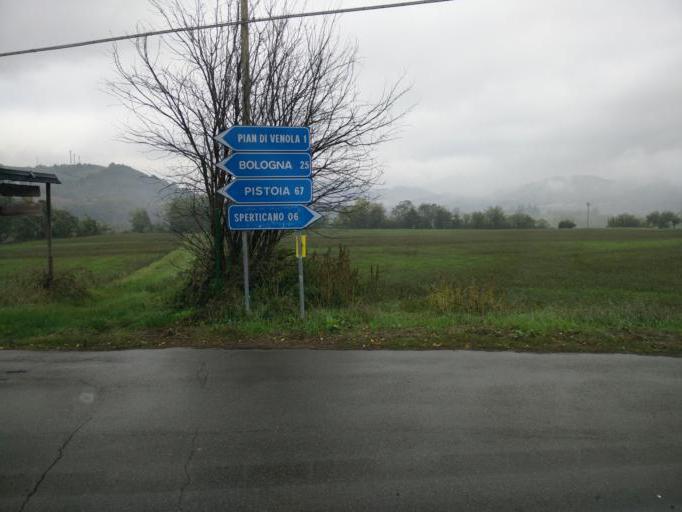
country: IT
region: Emilia-Romagna
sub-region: Provincia di Bologna
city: Marzabotto
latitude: 44.3274
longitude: 11.1914
